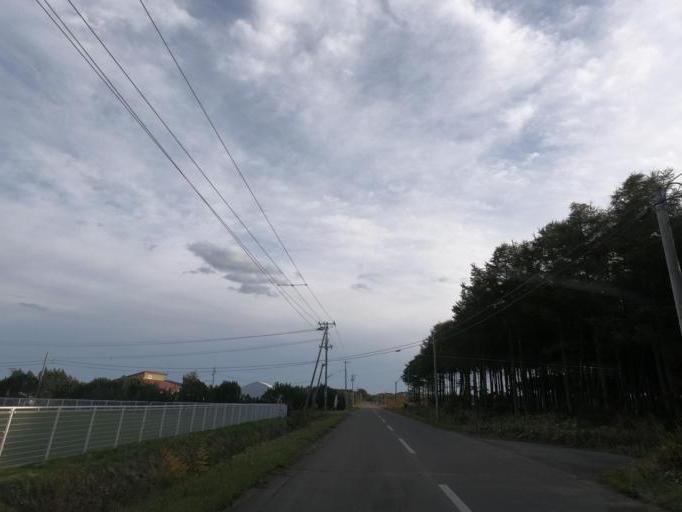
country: JP
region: Hokkaido
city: Obihiro
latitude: 42.4997
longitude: 143.4316
